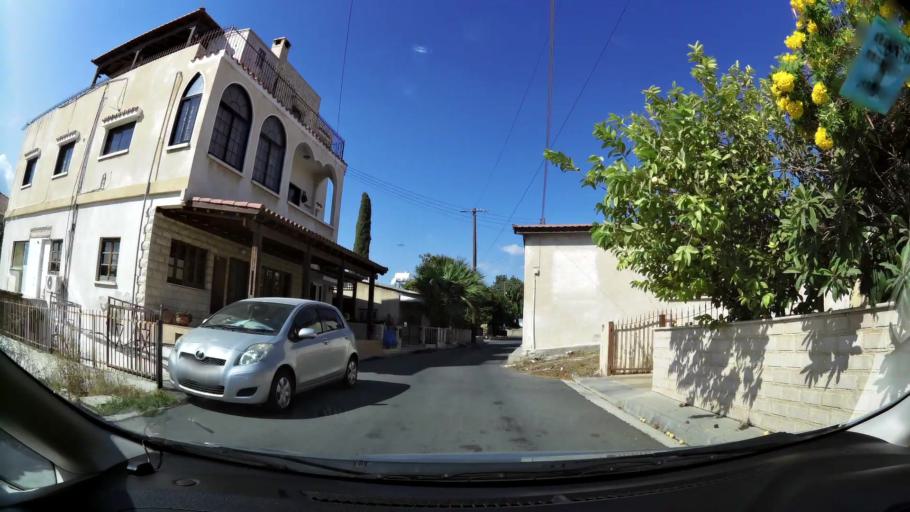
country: CY
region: Larnaka
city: Livadia
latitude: 34.9482
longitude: 33.6291
